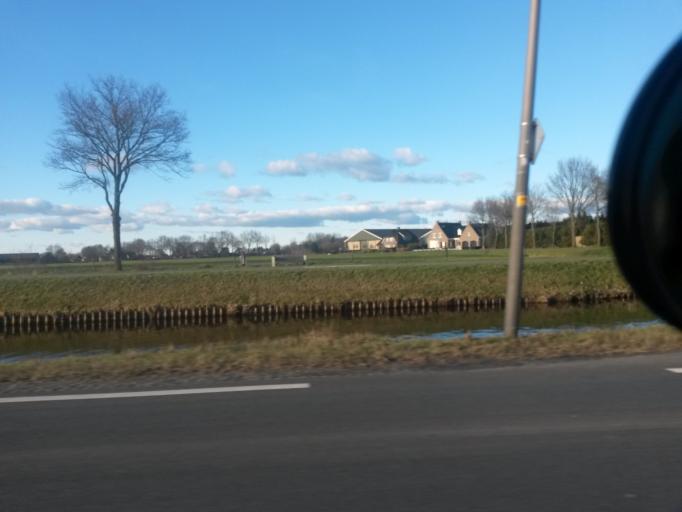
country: NL
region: Drenthe
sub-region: Gemeente Coevorden
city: Coevorden
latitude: 52.6540
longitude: 6.6551
